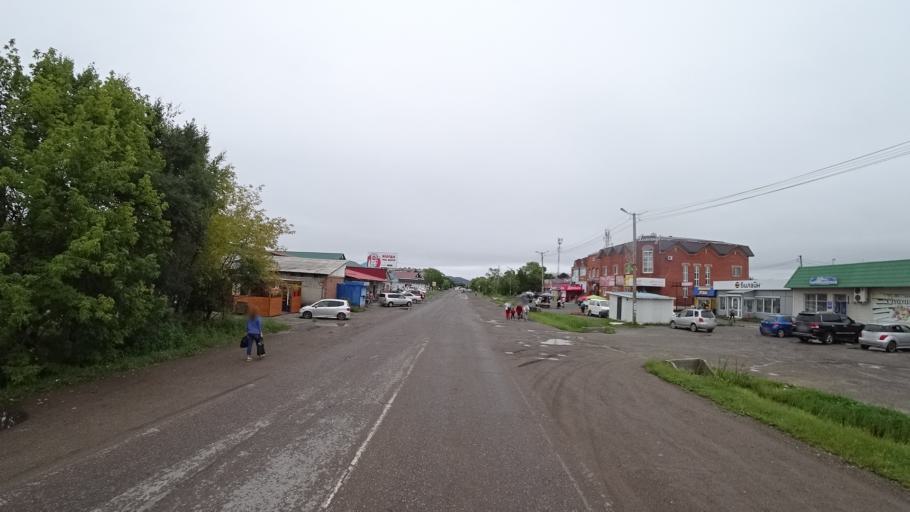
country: RU
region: Primorskiy
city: Monastyrishche
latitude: 44.2058
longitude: 132.4417
